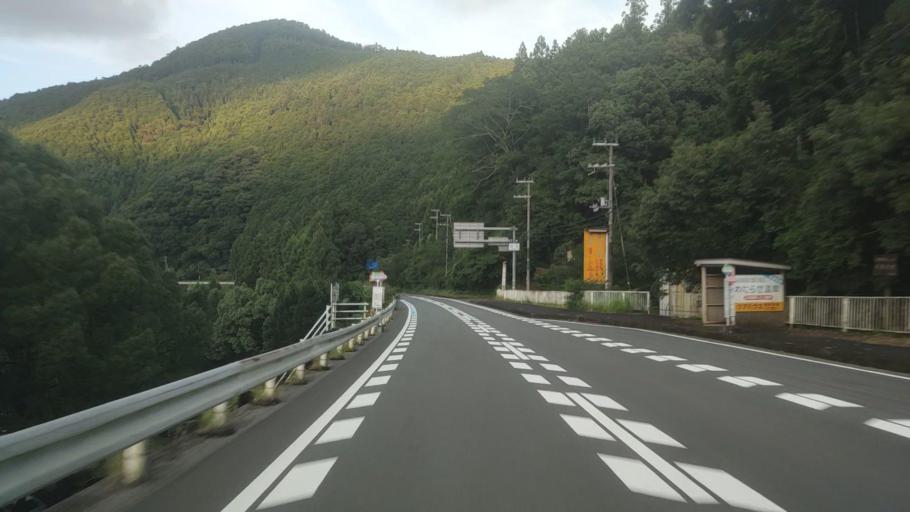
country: JP
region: Wakayama
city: Shingu
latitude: 33.8173
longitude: 135.7642
